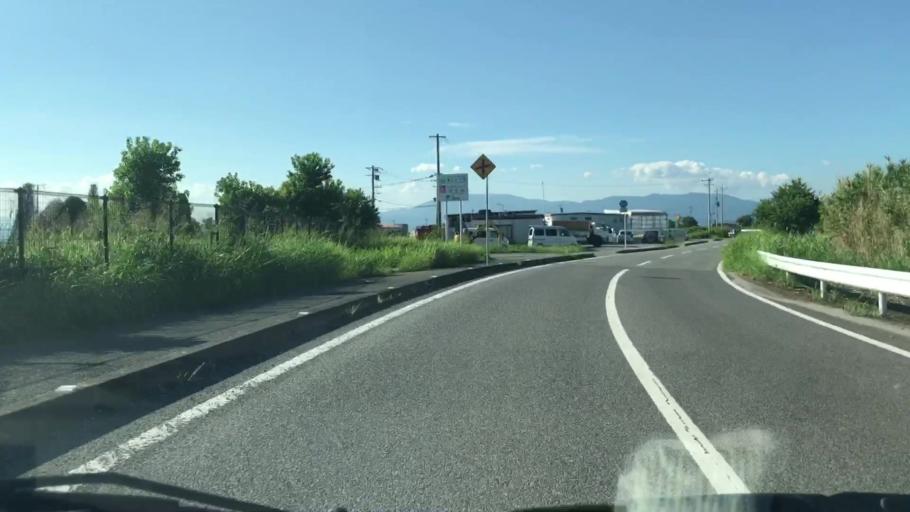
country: JP
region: Saga Prefecture
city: Okawa
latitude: 33.1869
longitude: 130.2900
